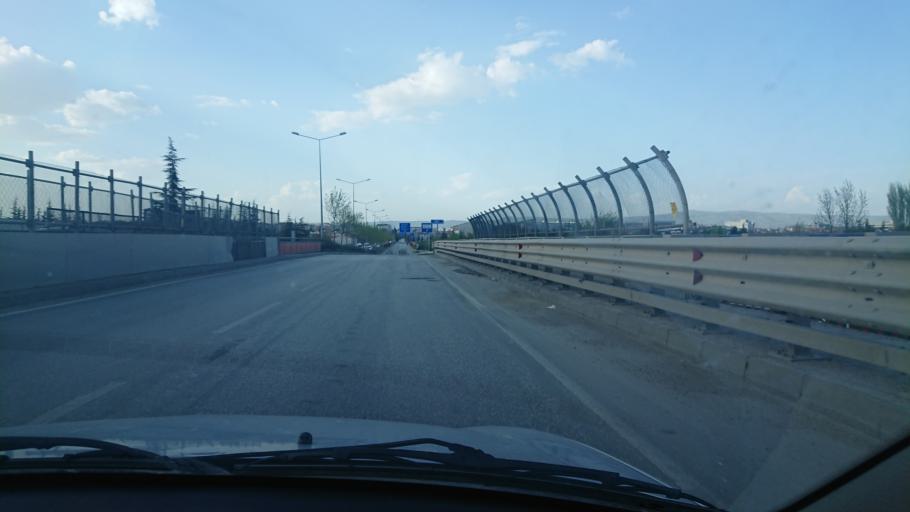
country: TR
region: Eskisehir
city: Eskisehir
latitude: 39.7756
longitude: 30.4840
